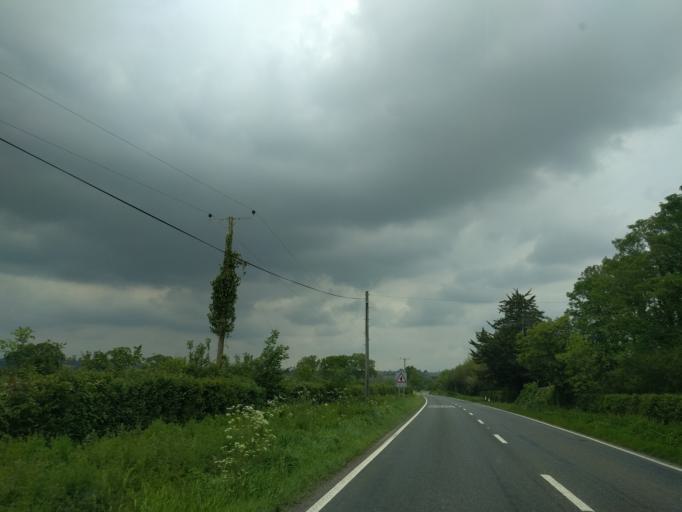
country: GB
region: England
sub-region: Somerset
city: Castle Cary
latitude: 51.1061
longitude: -2.5907
